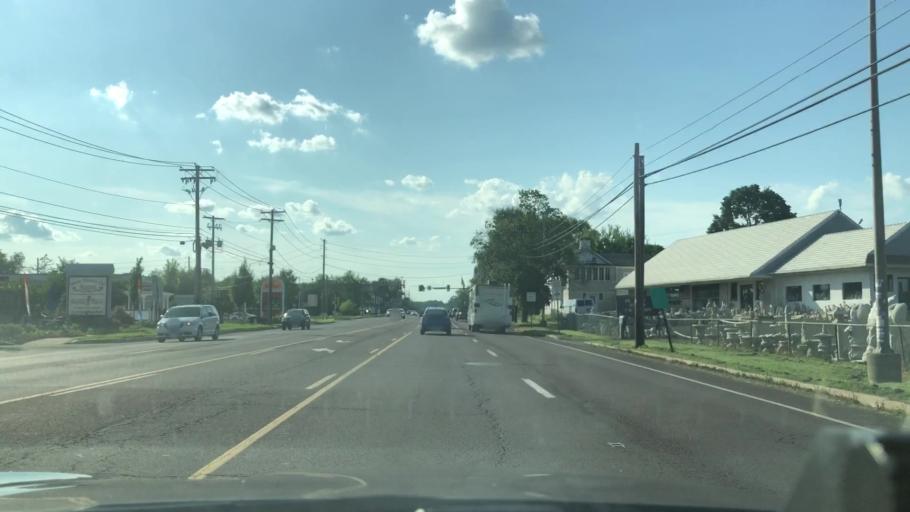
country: US
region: Pennsylvania
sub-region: Montgomery County
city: Hatfield
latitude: 40.2977
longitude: -75.2827
